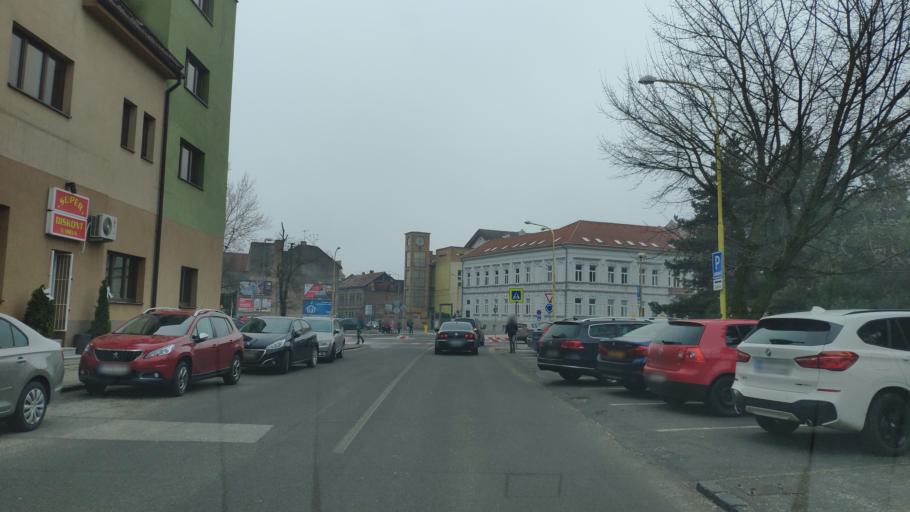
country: SK
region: Kosicky
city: Kosice
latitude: 48.7291
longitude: 21.2606
